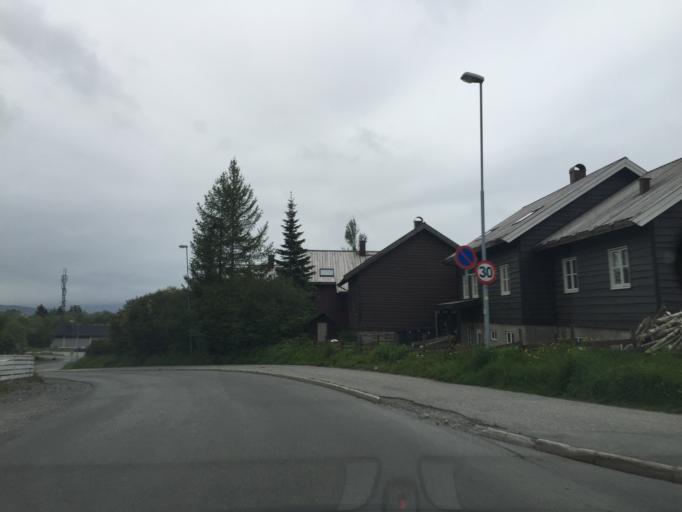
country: NO
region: Nordland
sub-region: Bodo
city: Lopsmarka
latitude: 67.2909
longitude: 14.5851
